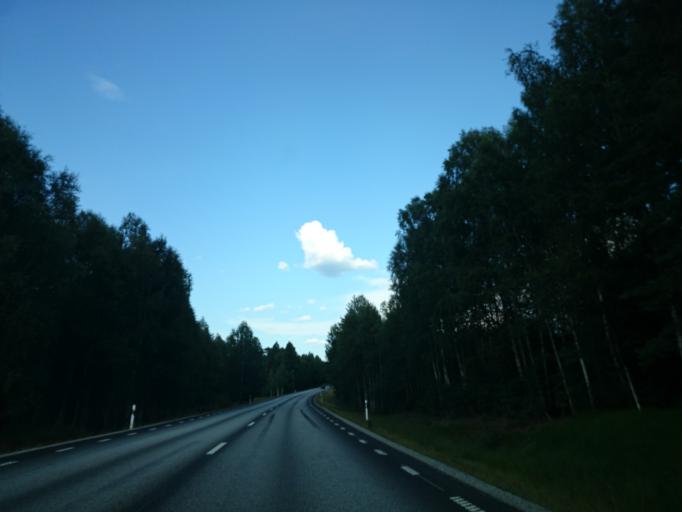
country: SE
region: OErebro
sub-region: Lindesbergs Kommun
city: Lindesberg
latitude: 59.6882
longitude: 15.3343
